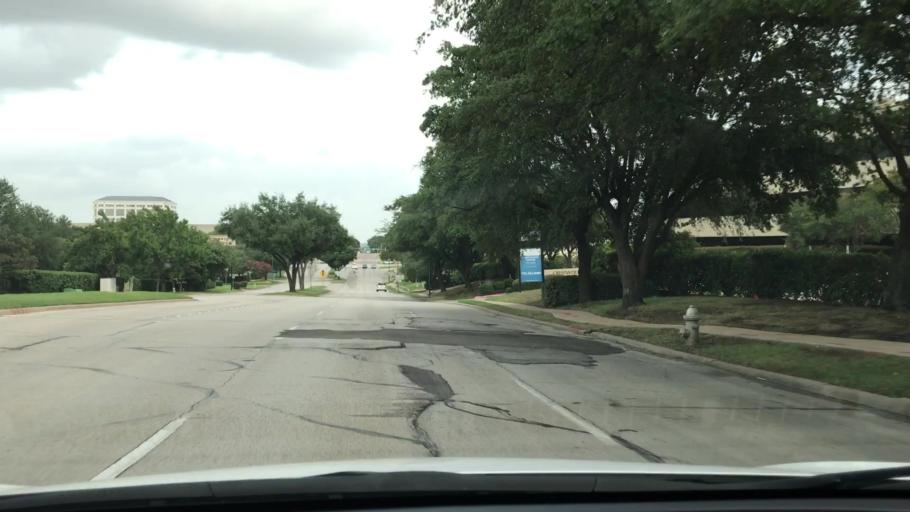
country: US
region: Texas
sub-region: Dallas County
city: Irving
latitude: 32.8849
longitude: -96.9678
